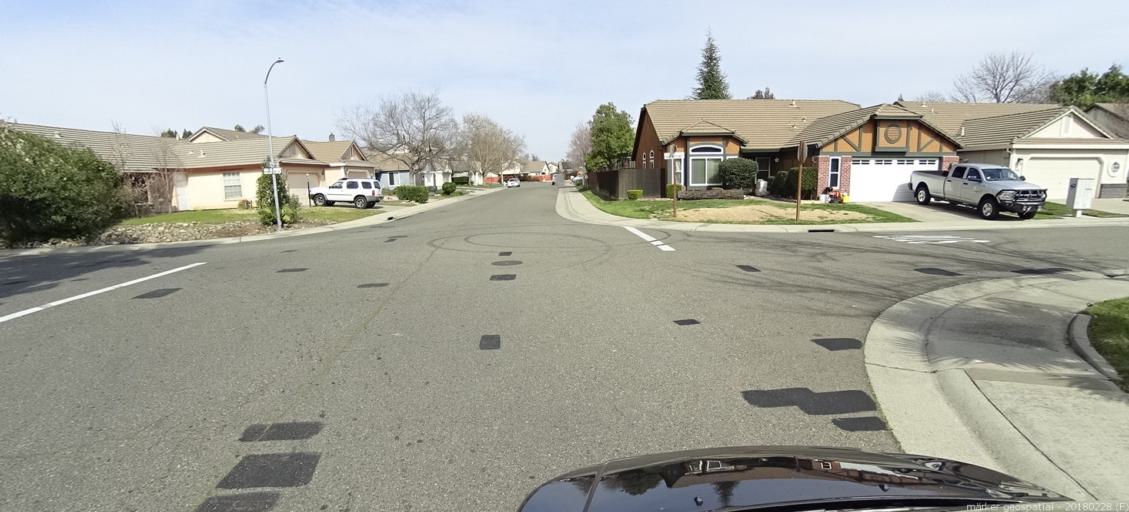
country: US
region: California
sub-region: Sacramento County
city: Antelope
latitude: 38.7210
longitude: -121.3440
